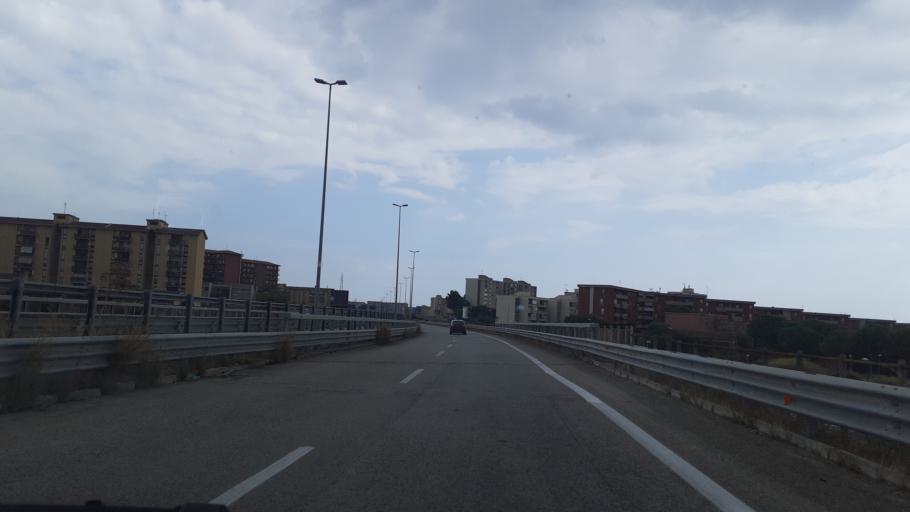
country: IT
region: Sicily
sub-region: Catania
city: Catania
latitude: 37.4784
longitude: 15.0463
